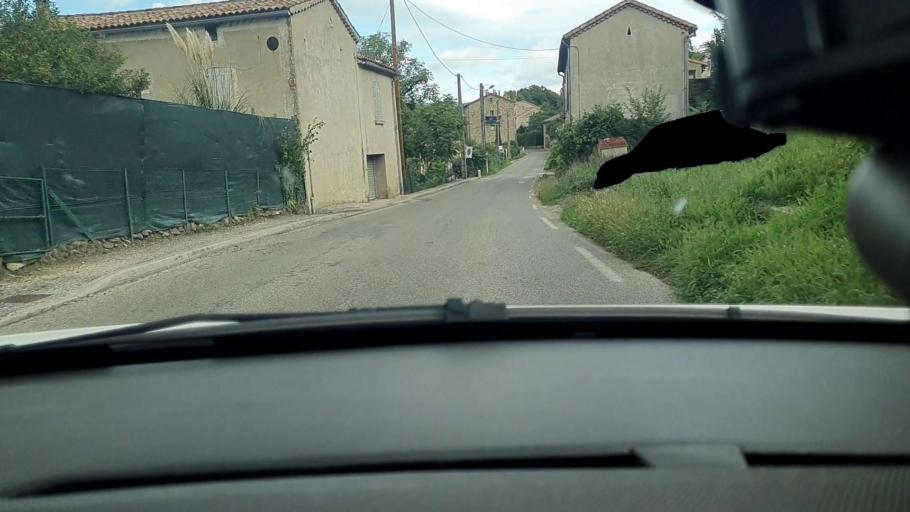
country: FR
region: Languedoc-Roussillon
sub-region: Departement du Gard
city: Besseges
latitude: 44.3025
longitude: 4.1290
